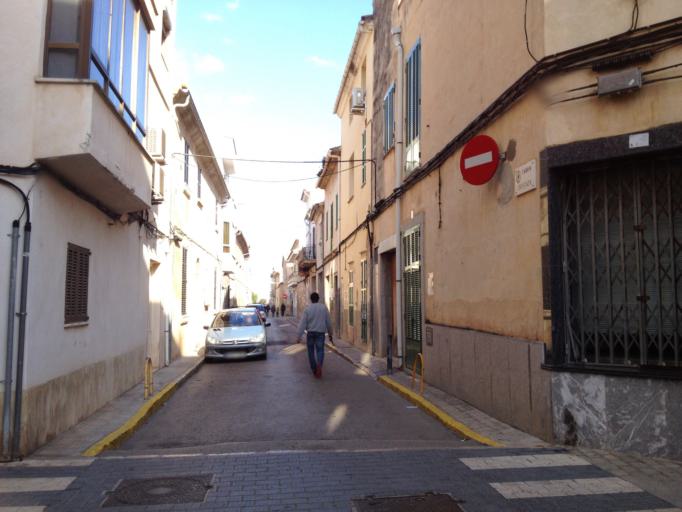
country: ES
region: Balearic Islands
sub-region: Illes Balears
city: sa Pobla
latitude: 39.7708
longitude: 3.0248
